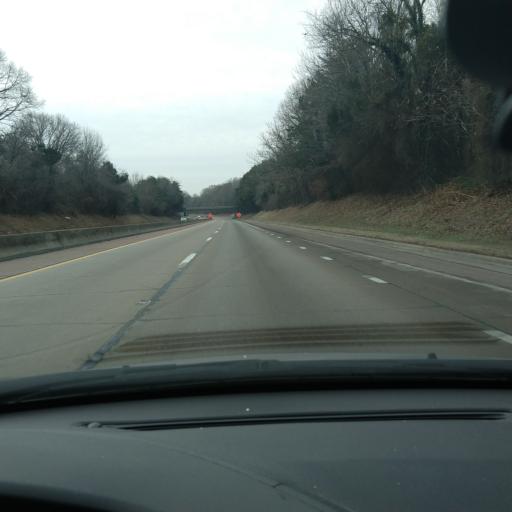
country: US
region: North Carolina
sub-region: Forsyth County
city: Winston-Salem
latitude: 36.0441
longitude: -80.2384
